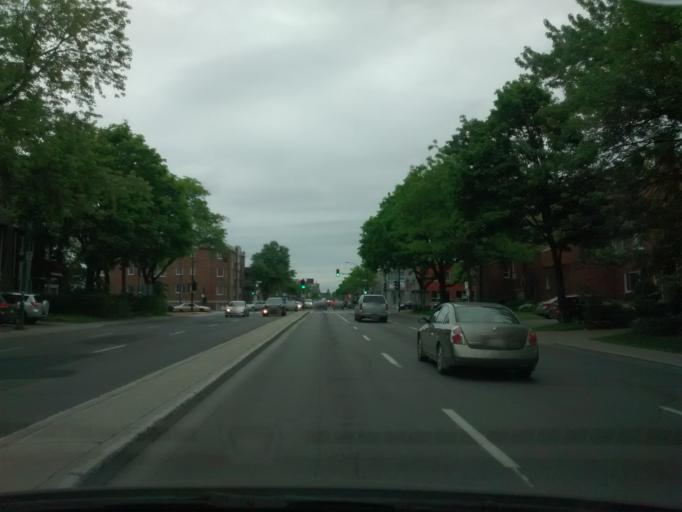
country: CA
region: Quebec
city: Mont-Royal
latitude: 45.5232
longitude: -73.6264
